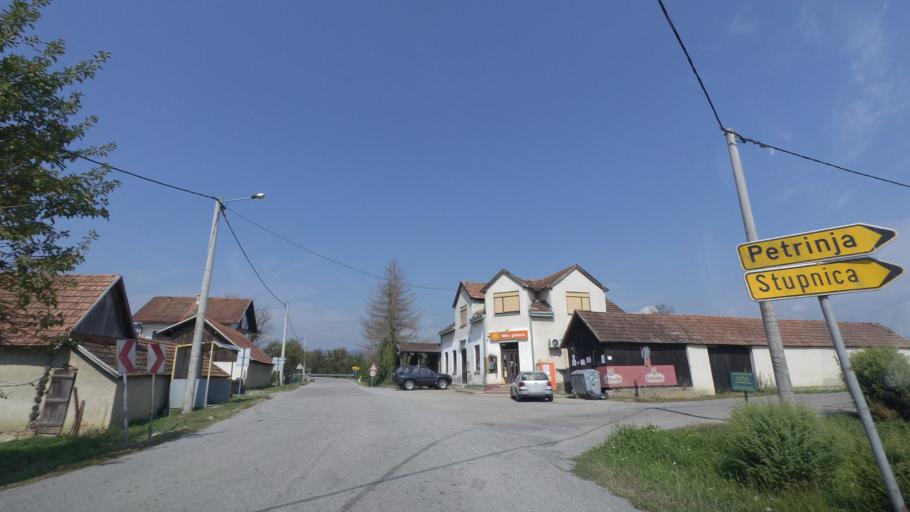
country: HR
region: Sisacko-Moslavacka
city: Dvor
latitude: 45.1147
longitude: 16.2750
